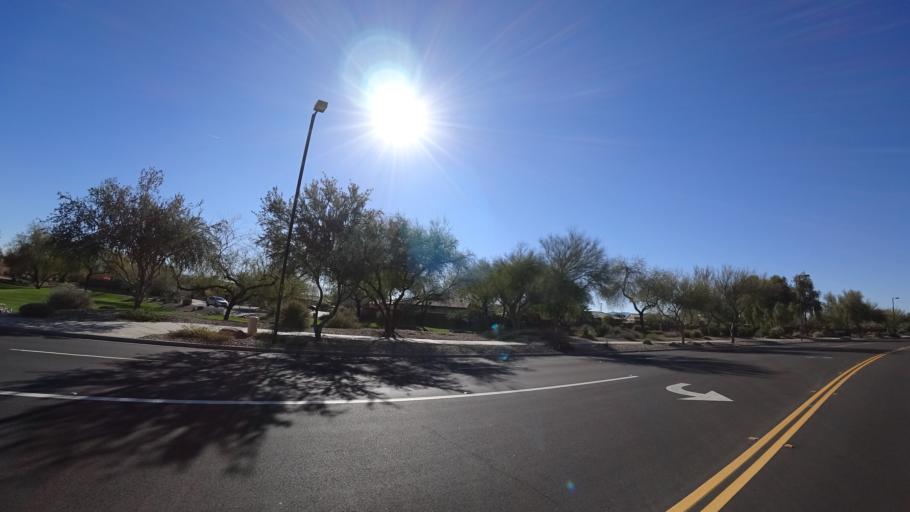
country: US
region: Arizona
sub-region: Maricopa County
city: Sun City West
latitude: 33.6554
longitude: -112.3798
